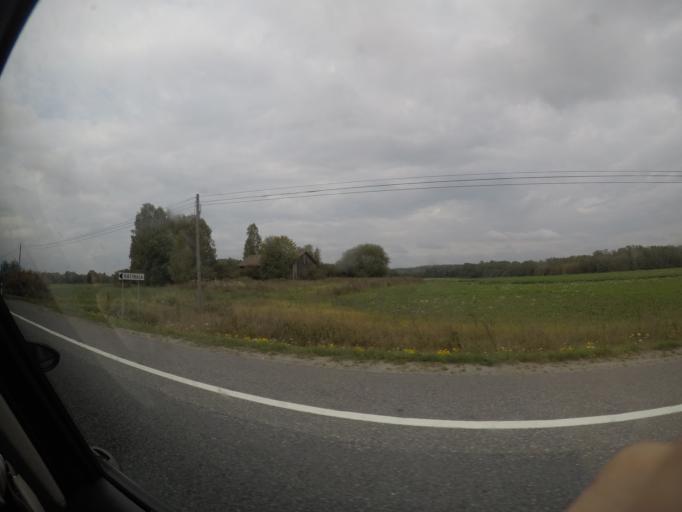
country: FI
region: Haeme
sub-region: Haemeenlinna
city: Haemeenlinna
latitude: 61.0320
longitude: 24.4160
